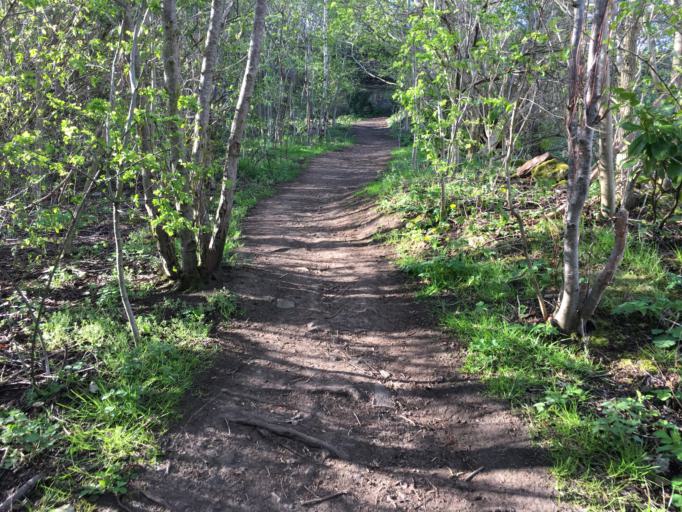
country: GB
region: Scotland
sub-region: Edinburgh
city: Colinton
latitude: 55.9171
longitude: -3.2310
